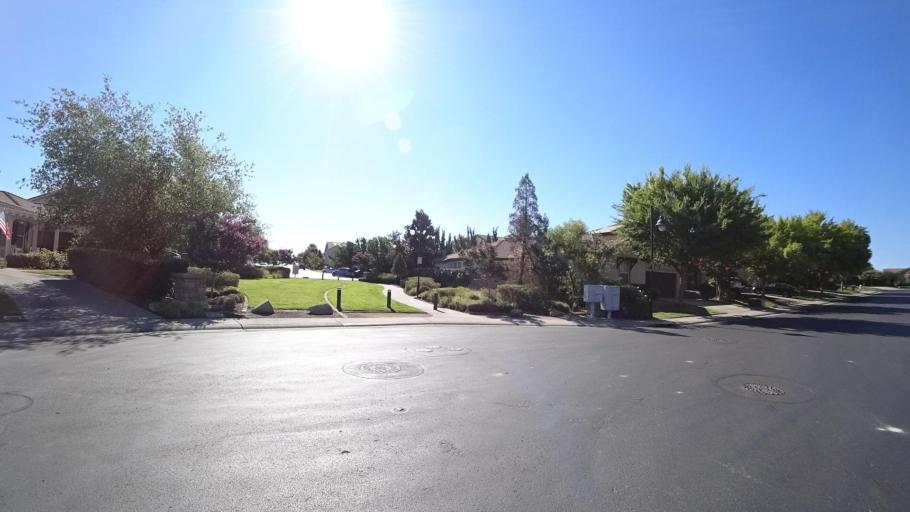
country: US
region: California
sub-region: Placer County
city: Lincoln
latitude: 38.8388
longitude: -121.2872
